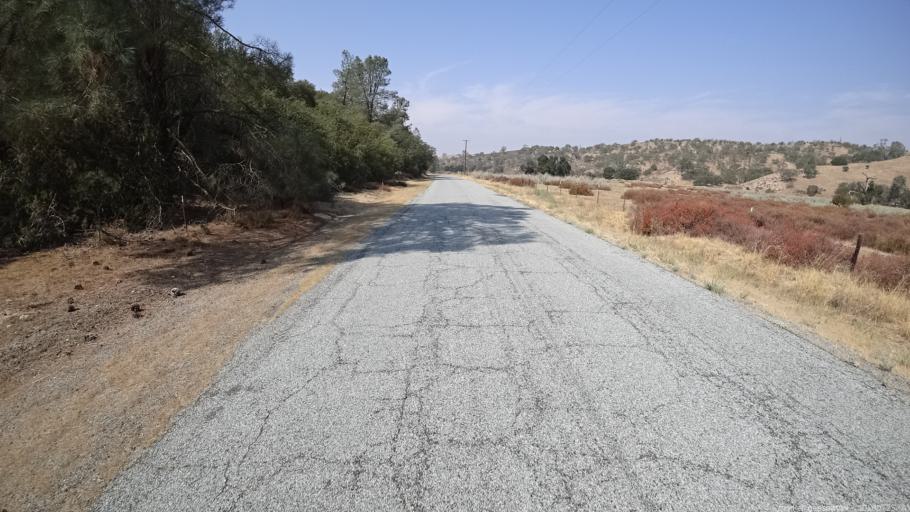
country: US
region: California
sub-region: San Luis Obispo County
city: San Miguel
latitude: 35.8562
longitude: -120.6020
